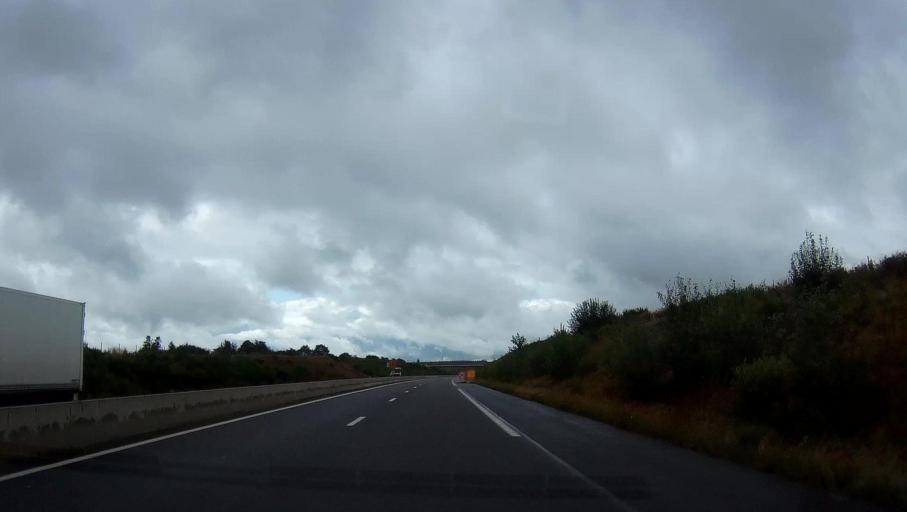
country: FR
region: Champagne-Ardenne
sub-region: Departement des Ardennes
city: Rocroi
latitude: 49.8917
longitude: 4.5203
